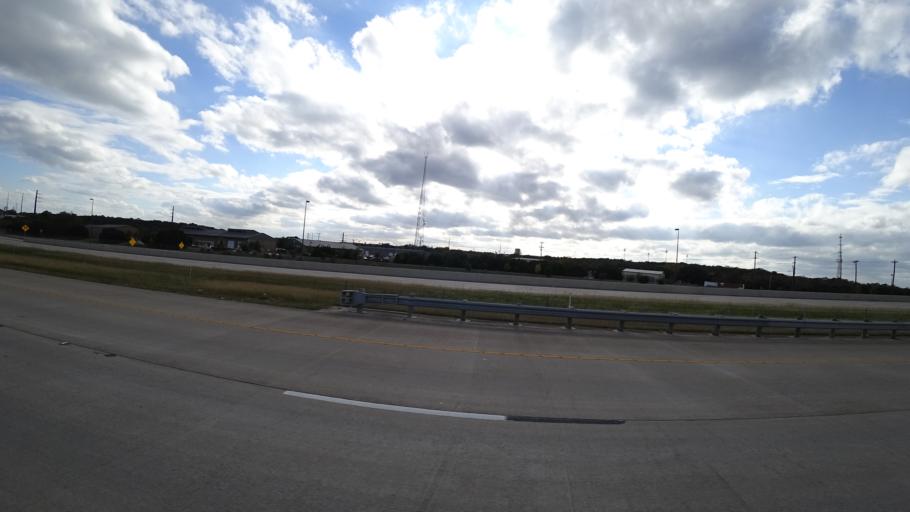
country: US
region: Texas
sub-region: Williamson County
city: Cedar Park
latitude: 30.4996
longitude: -97.8048
